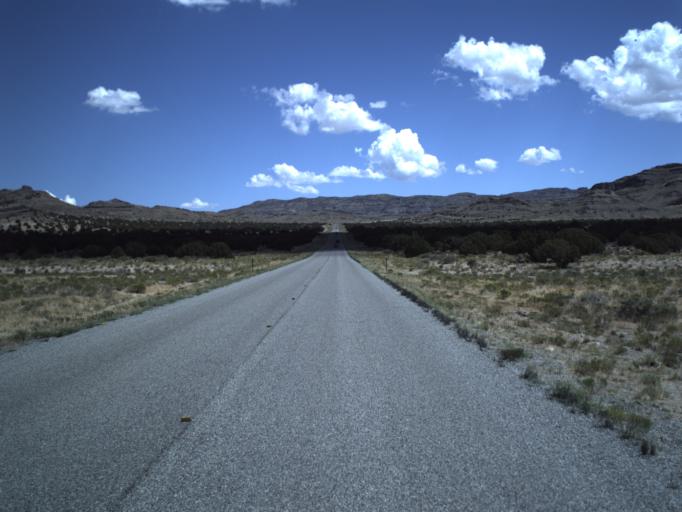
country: US
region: Utah
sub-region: Beaver County
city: Milford
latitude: 39.0701
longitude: -113.7288
